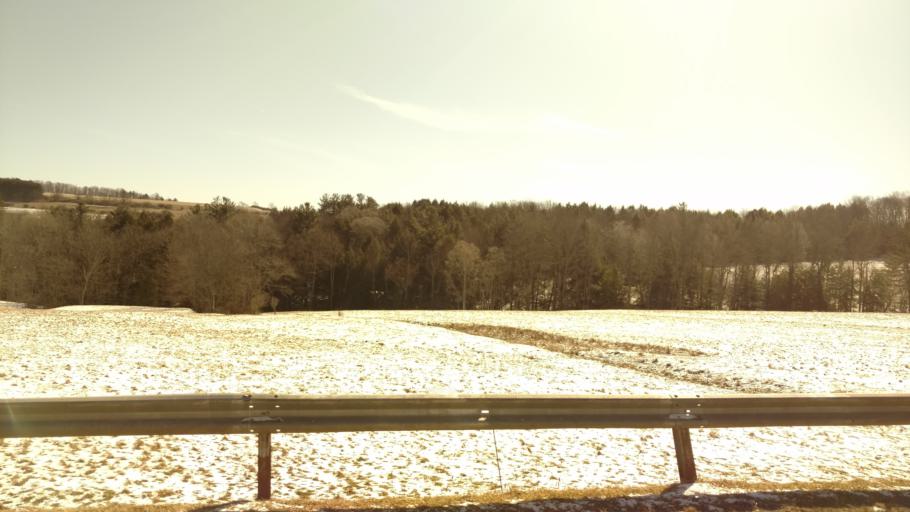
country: US
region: New York
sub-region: Allegany County
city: Wellsville
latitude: 42.0914
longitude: -77.9590
